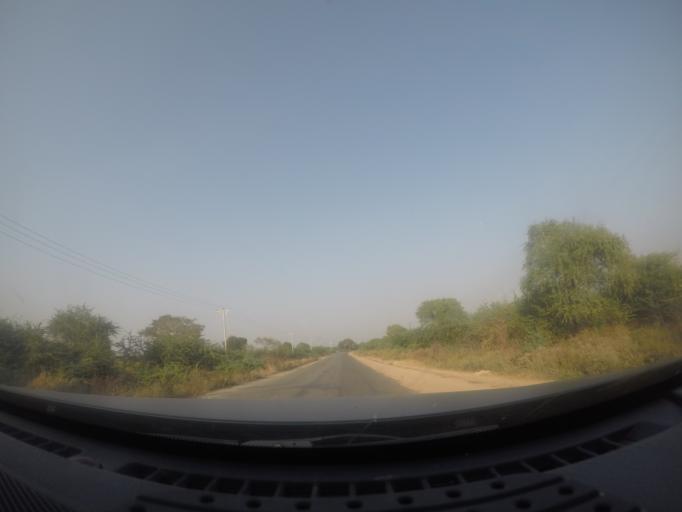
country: MM
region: Mandalay
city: Yamethin
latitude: 20.6627
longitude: 96.1207
